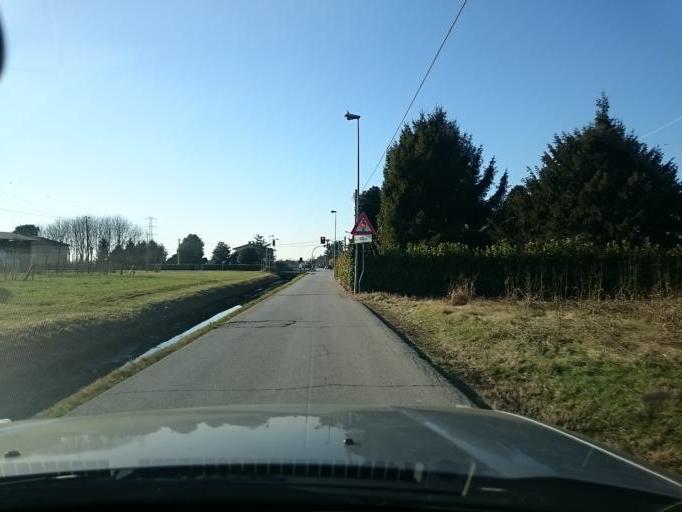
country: IT
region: Veneto
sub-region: Provincia di Venezia
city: Mira Taglio
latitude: 45.4334
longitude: 12.1583
